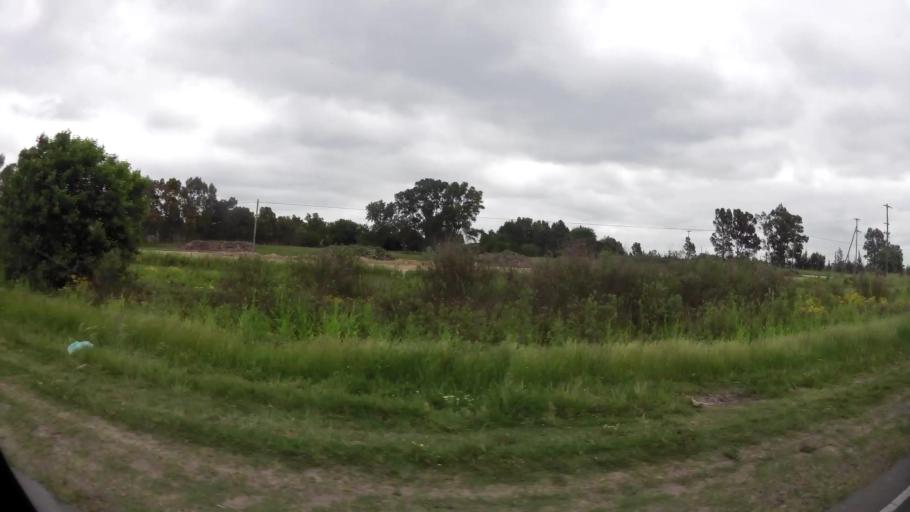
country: AR
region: Buenos Aires
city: Guernica
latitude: -34.9480
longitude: -58.4659
